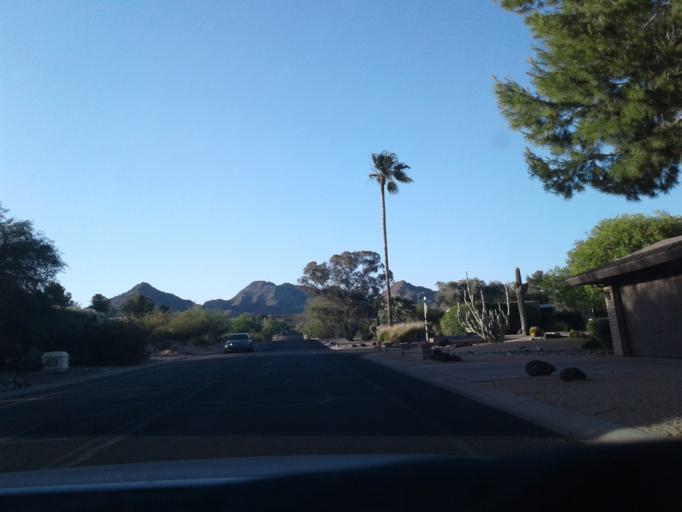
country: US
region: Arizona
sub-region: Maricopa County
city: Paradise Valley
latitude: 33.5200
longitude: -111.9952
